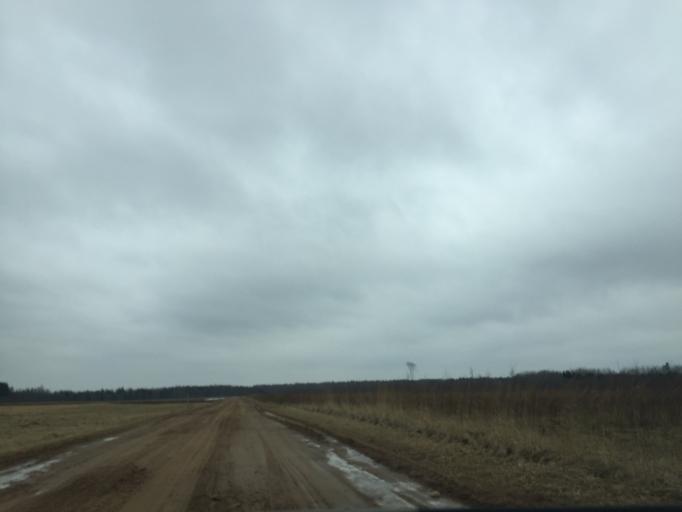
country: LV
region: Lielvarde
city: Lielvarde
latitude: 56.7574
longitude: 24.8024
